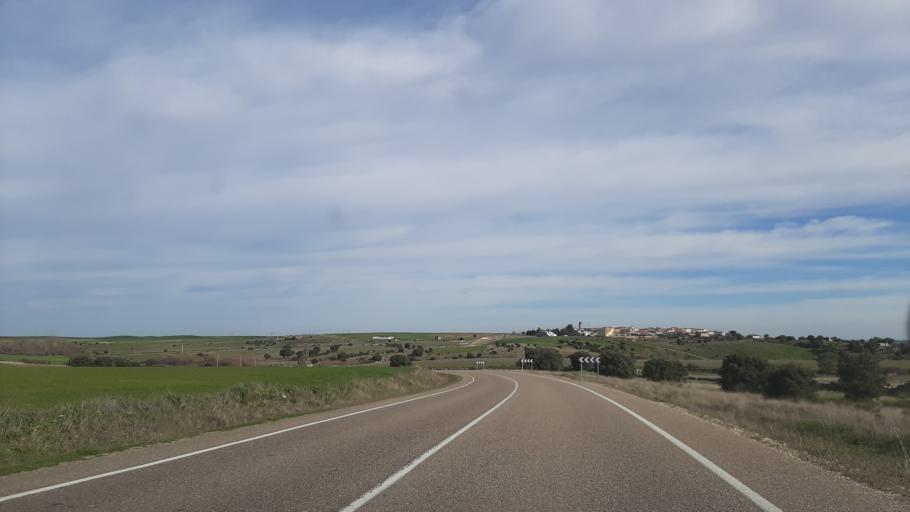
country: ES
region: Castille and Leon
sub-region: Provincia de Salamanca
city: Juzbado
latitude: 41.0810
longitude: -5.8756
